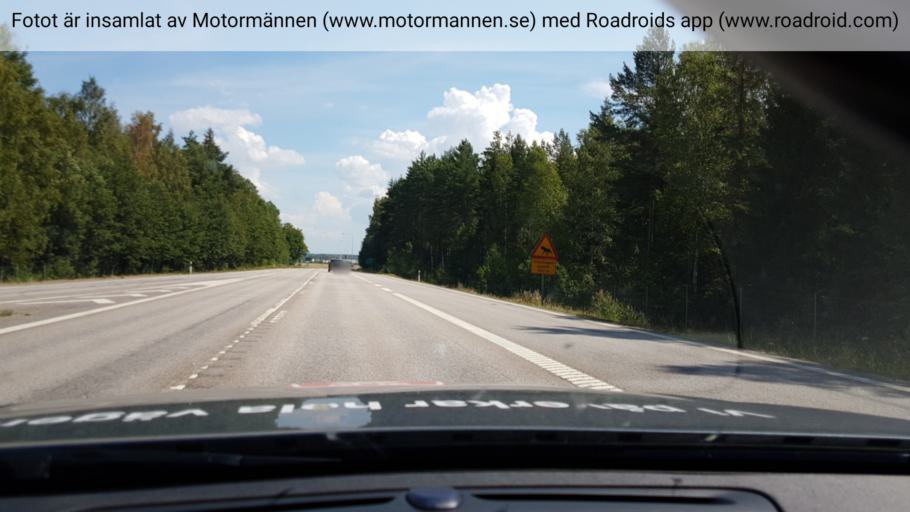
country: SE
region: OErebro
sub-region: Hallsbergs Kommun
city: Hallsberg
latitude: 59.1027
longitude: 15.0670
